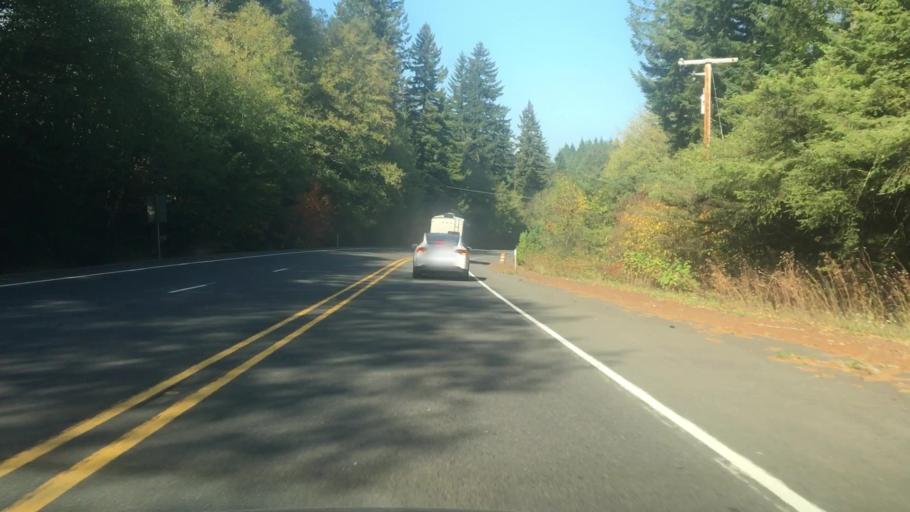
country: US
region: Oregon
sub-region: Polk County
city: Grand Ronde
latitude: 45.0662
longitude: -123.7289
